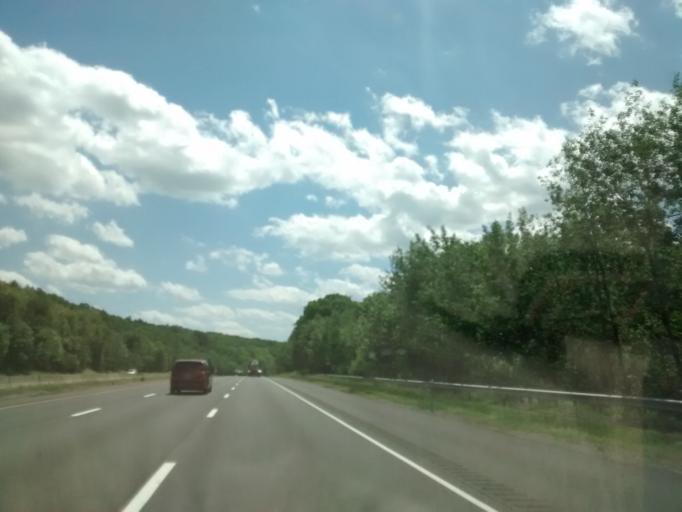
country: US
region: Connecticut
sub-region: Tolland County
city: Stafford Springs
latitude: 41.9103
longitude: -72.2710
